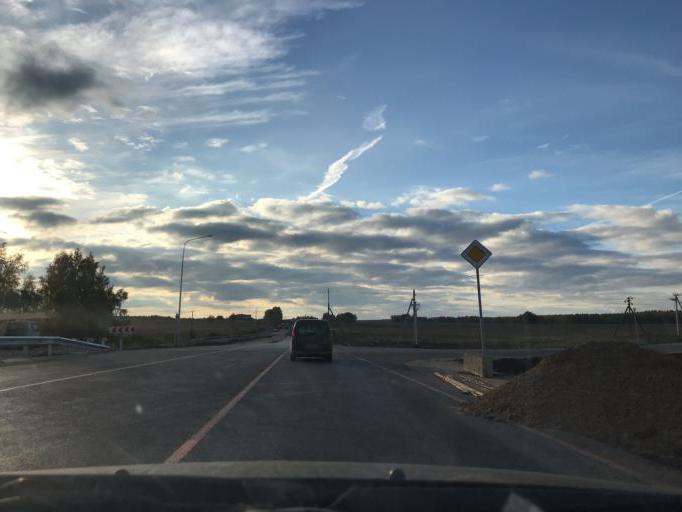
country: RU
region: Kaluga
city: Kurovskoye
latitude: 54.5284
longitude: 35.9805
